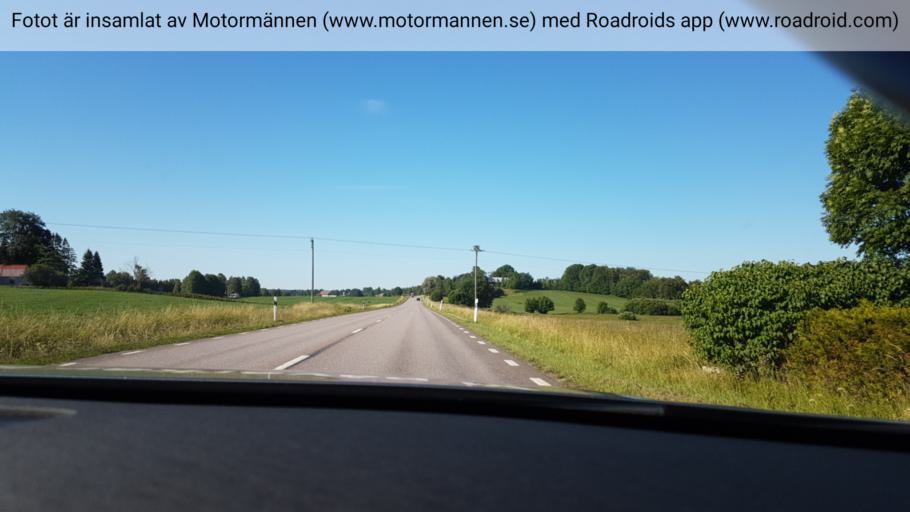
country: SE
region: Vaestra Goetaland
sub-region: Falkopings Kommun
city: Falkoeping
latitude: 58.1059
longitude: 13.5357
